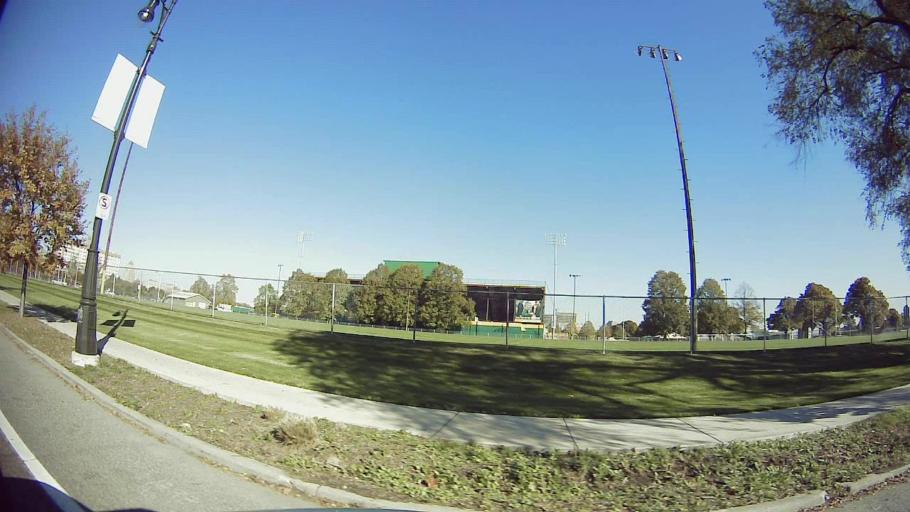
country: US
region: Michigan
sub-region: Wayne County
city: Detroit
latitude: 42.3546
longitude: -83.0800
